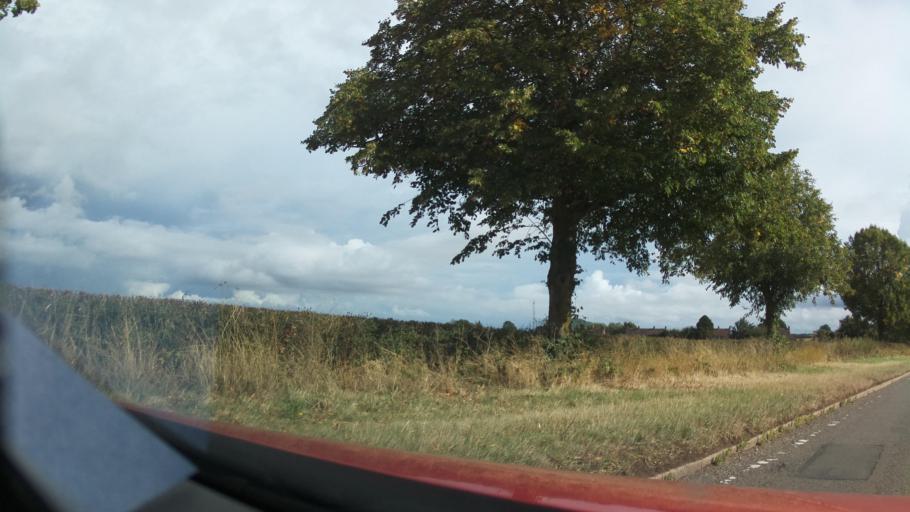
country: GB
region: England
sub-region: Telford and Wrekin
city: Madeley
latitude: 52.6046
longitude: -2.4055
